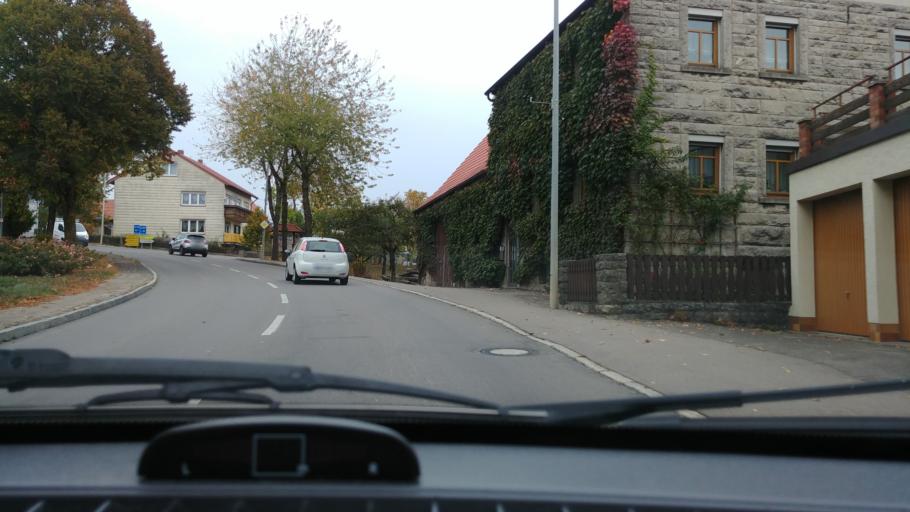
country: DE
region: Baden-Wuerttemberg
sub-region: Regierungsbezirk Stuttgart
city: Wallhausen
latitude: 49.2127
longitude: 10.0646
